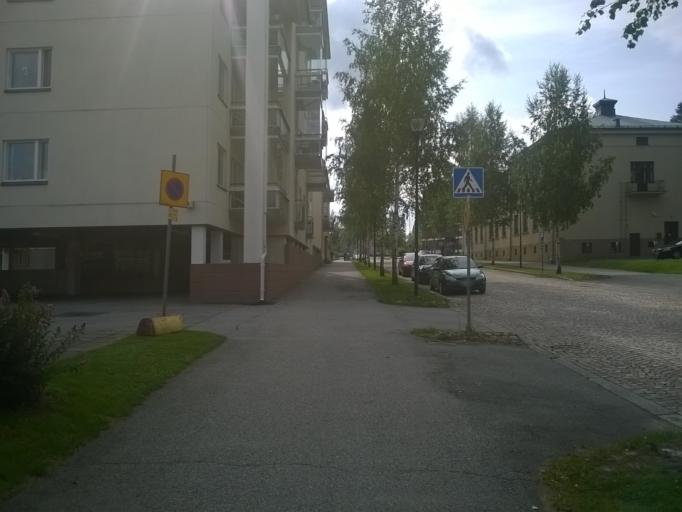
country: FI
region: Kainuu
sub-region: Kajaani
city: Kajaani
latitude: 64.2223
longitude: 27.7382
